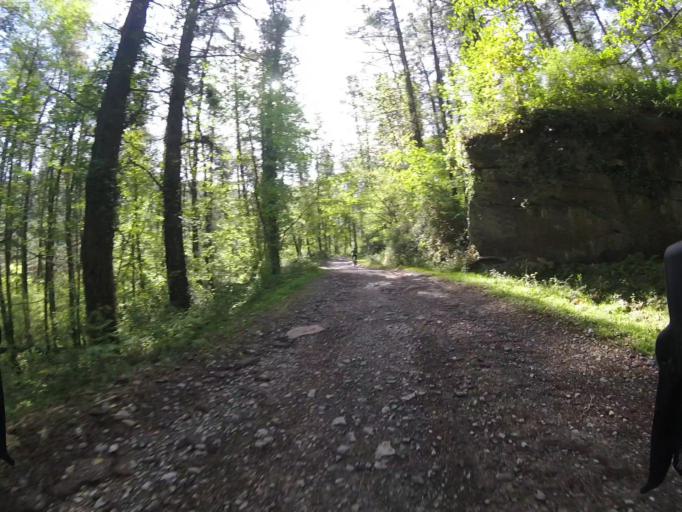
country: ES
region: Basque Country
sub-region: Provincia de Guipuzcoa
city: Urnieta
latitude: 43.2109
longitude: -1.9819
